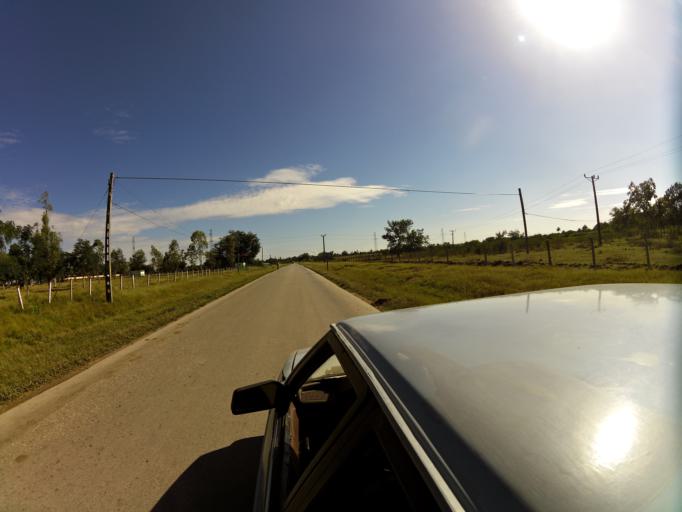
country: CU
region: Las Tunas
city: Las Tunas
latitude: 20.9822
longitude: -76.8954
